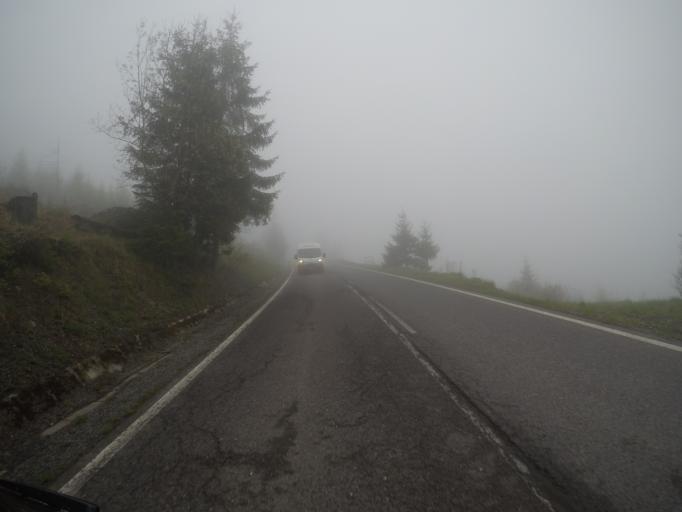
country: SK
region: Presovsky
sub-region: Okres Poprad
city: Strba
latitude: 49.1071
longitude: 20.0644
